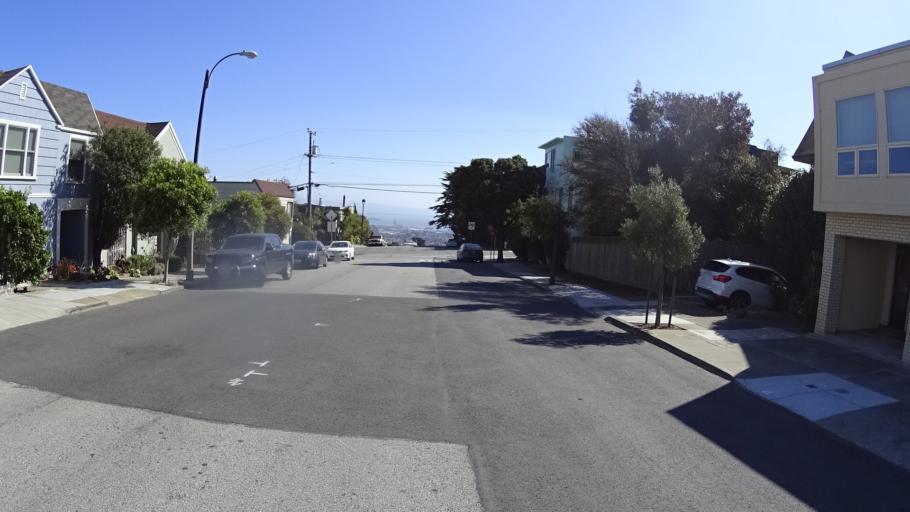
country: US
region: California
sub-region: San Francisco County
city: San Francisco
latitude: 37.7454
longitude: -122.4386
